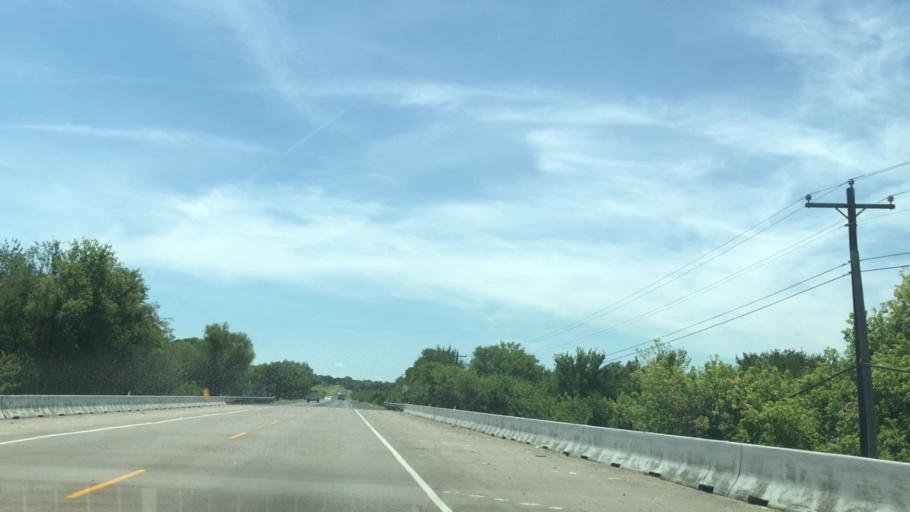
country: US
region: Texas
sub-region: Collin County
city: Lavon
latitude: 32.9852
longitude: -96.4668
